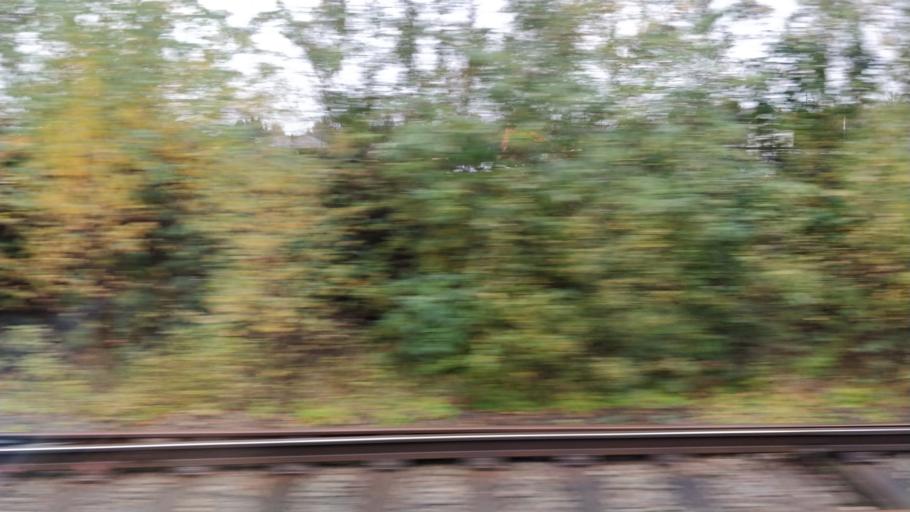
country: GB
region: England
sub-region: Borough of Wigan
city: Ince-in-Makerfield
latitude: 53.5464
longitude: -2.6419
